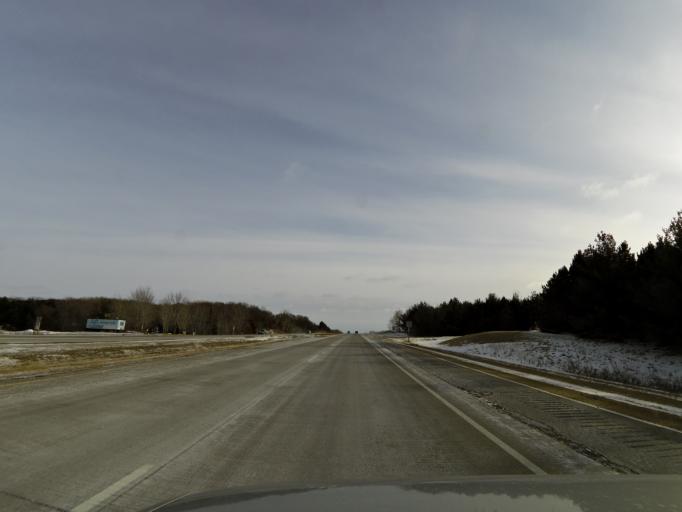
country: US
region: Minnesota
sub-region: Washington County
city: Lake Saint Croix Beach
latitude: 44.9285
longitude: -92.6815
